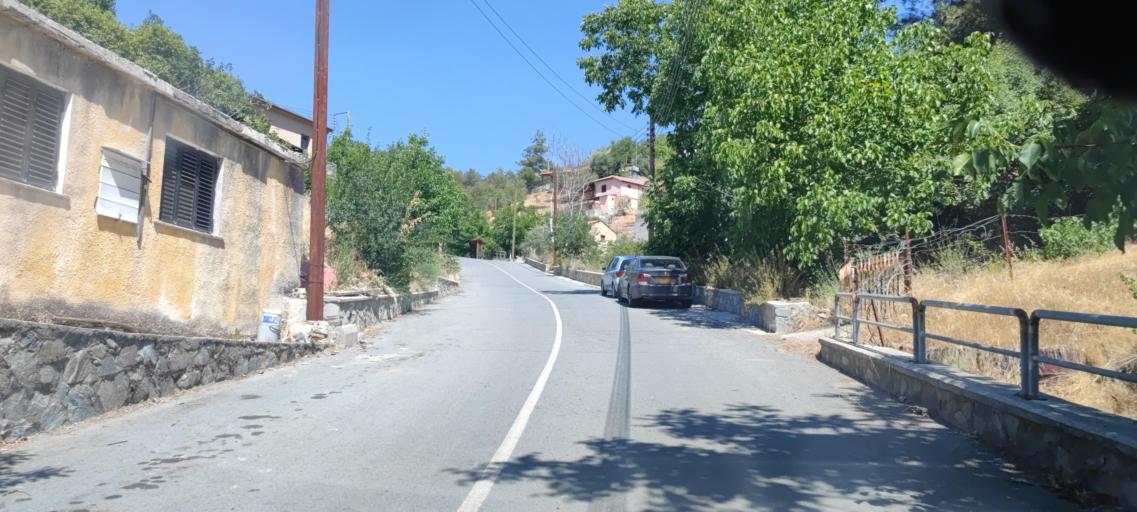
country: CY
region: Lefkosia
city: Kakopetria
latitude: 34.9322
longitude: 32.7950
